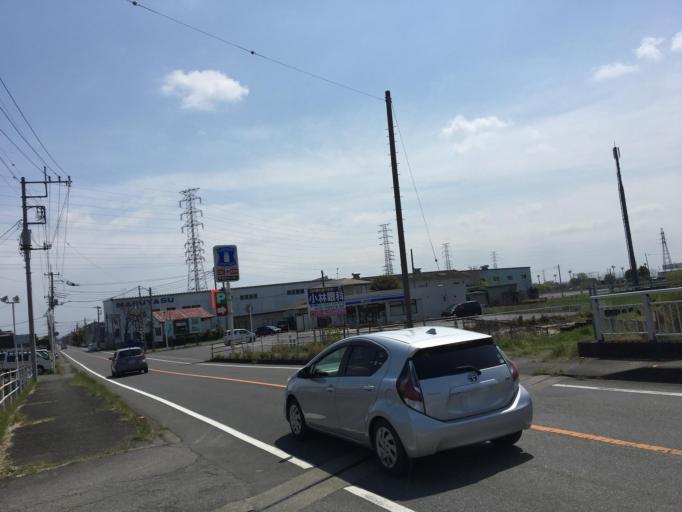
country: JP
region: Gunma
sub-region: Sawa-gun
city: Tamamura
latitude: 36.3035
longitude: 139.0953
